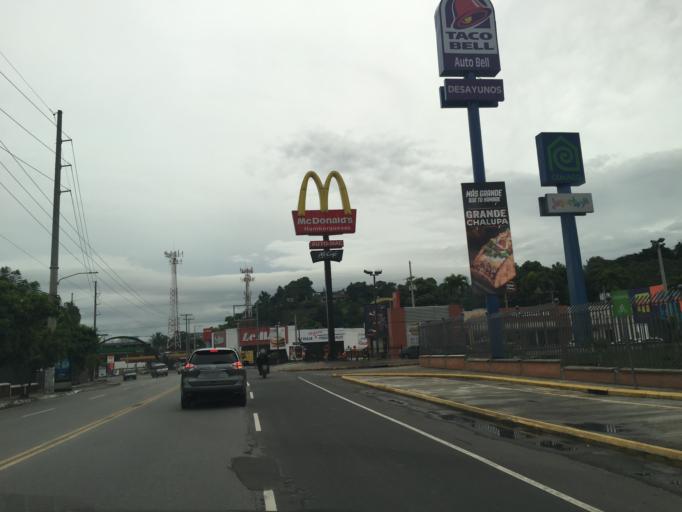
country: GT
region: Guatemala
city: Petapa
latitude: 14.5192
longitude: -90.5641
